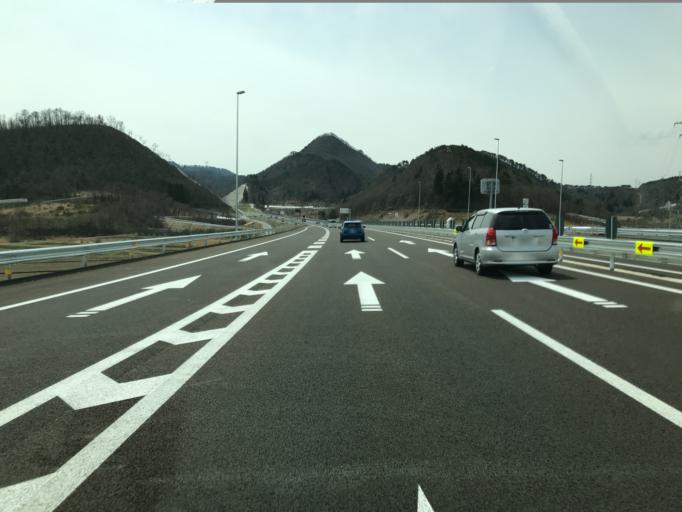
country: JP
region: Yamagata
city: Kaminoyama
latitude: 38.1263
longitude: 140.2557
